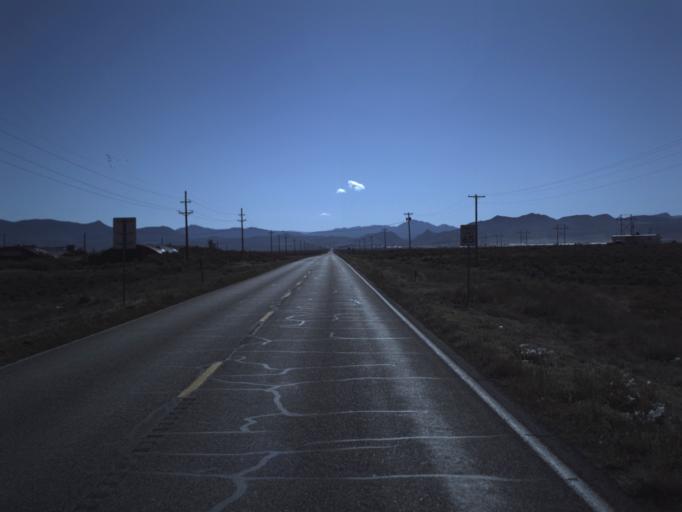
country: US
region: Utah
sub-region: Washington County
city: Enterprise
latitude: 37.7062
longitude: -113.6471
